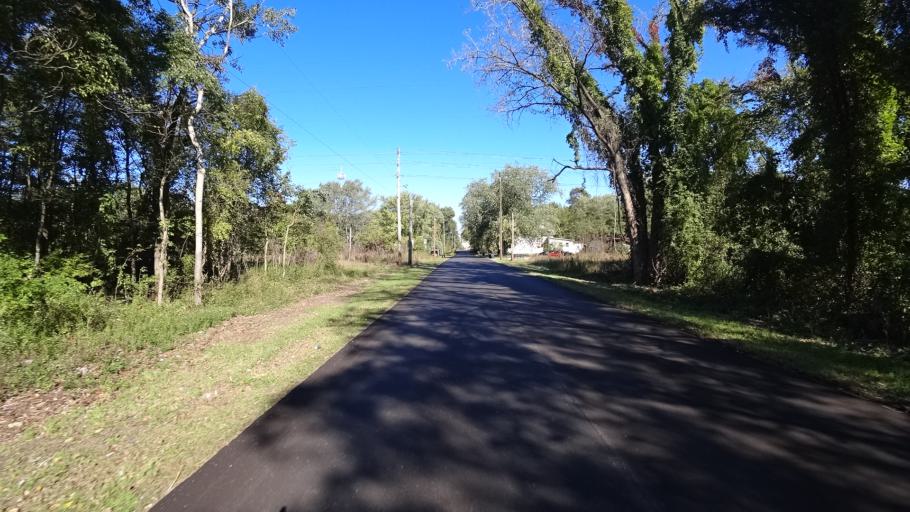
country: US
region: Indiana
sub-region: LaPorte County
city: Michigan City
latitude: 41.6976
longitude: -86.9140
